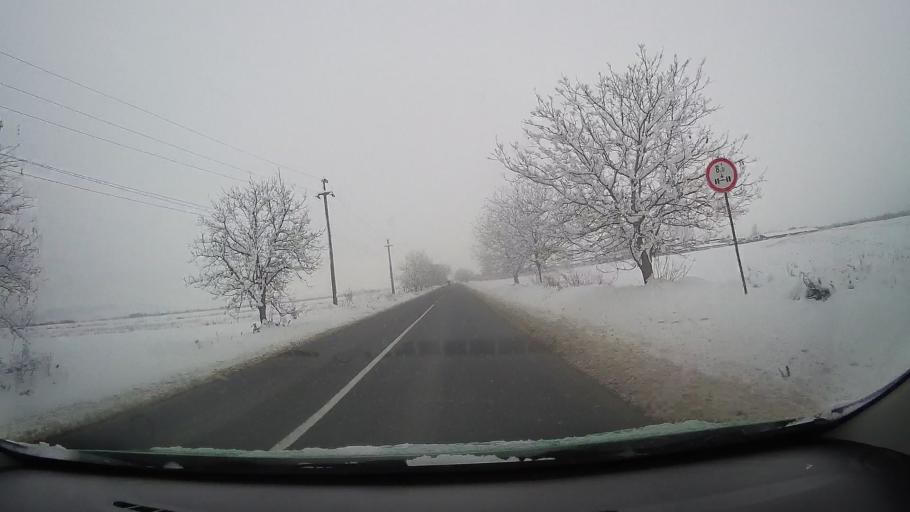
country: RO
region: Sibiu
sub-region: Comuna Orlat
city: Orlat
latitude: 45.7612
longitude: 23.9869
